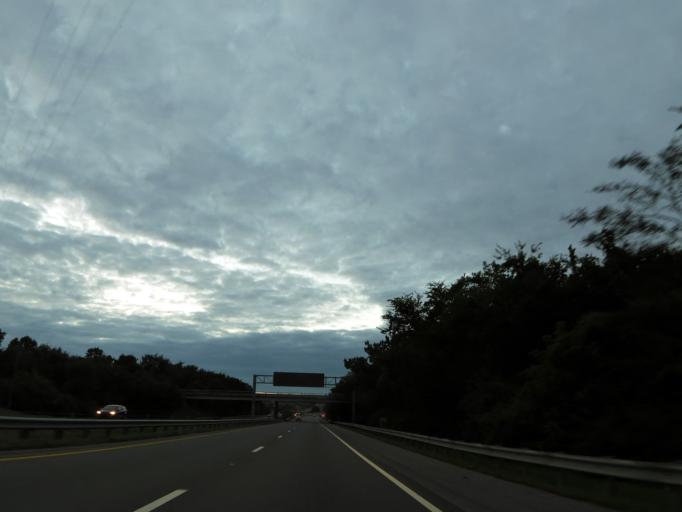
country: US
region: Tennessee
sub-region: Davidson County
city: Belle Meade
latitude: 36.1627
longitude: -86.8675
